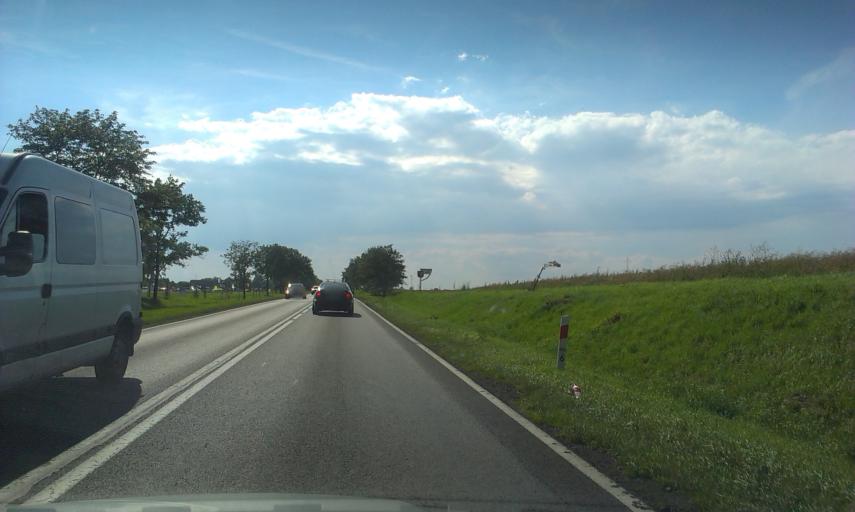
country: PL
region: Kujawsko-Pomorskie
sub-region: Powiat nakielski
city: Slesin
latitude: 53.1674
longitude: 17.7535
